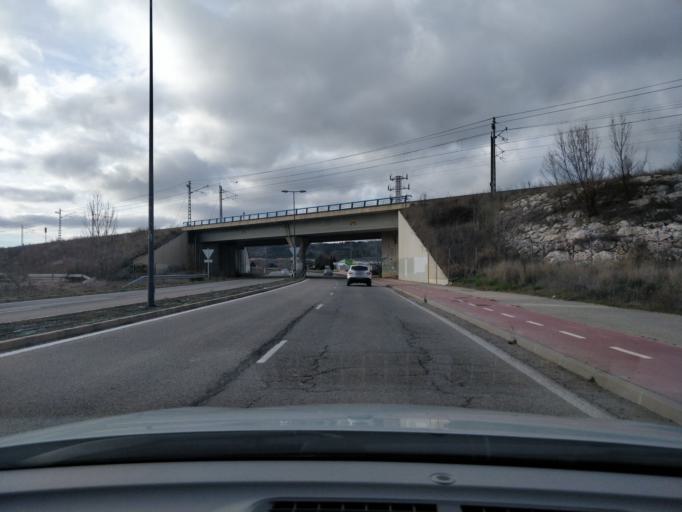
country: ES
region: Castille and Leon
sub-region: Provincia de Burgos
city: Villalbilla de Burgos
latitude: 42.3570
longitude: -3.7596
